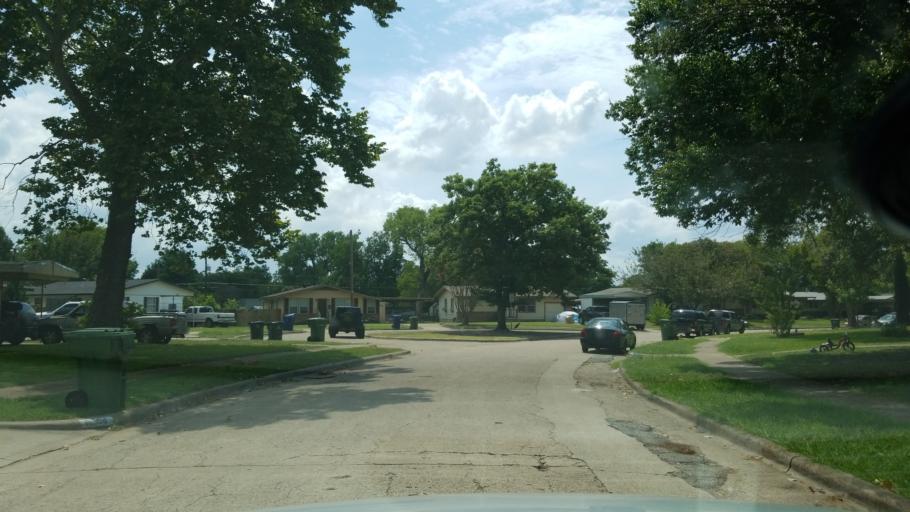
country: US
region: Texas
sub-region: Dallas County
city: Garland
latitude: 32.9213
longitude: -96.6565
